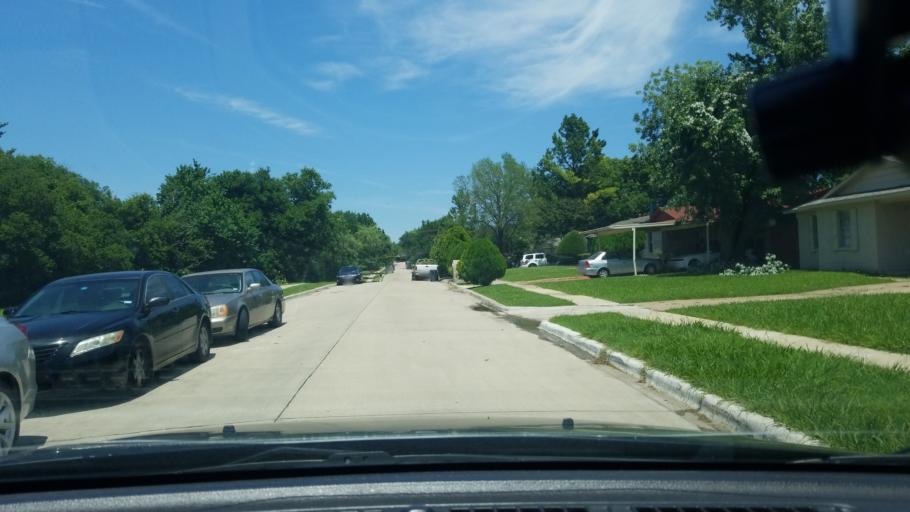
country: US
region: Texas
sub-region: Dallas County
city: Mesquite
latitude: 32.7852
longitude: -96.6219
